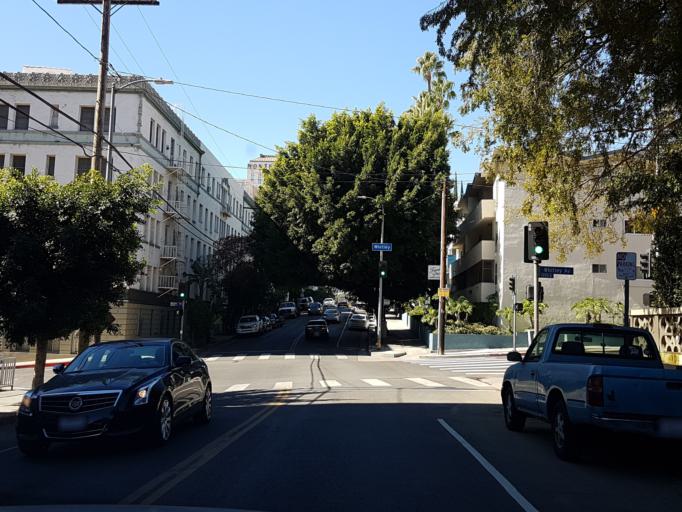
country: US
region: California
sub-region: Los Angeles County
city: Hollywood
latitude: 34.1053
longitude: -118.3330
